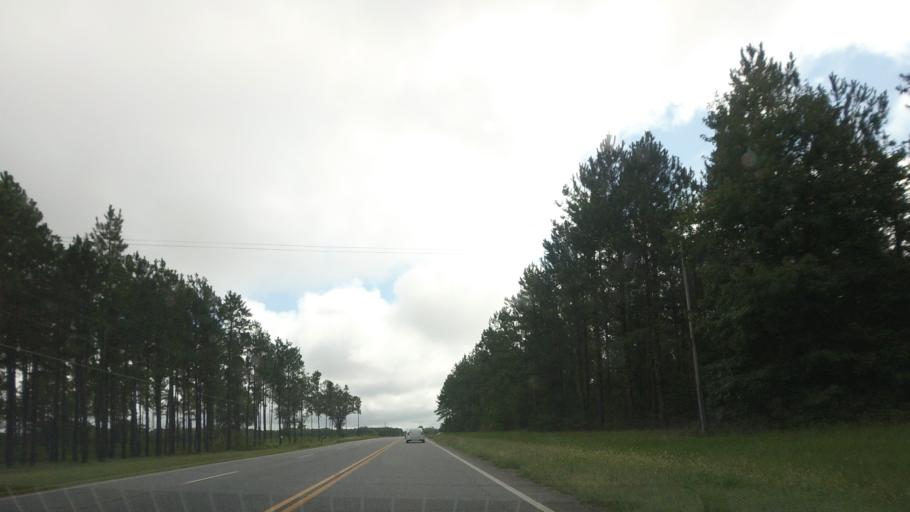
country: US
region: Georgia
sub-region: Laurens County
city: Dublin
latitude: 32.5505
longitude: -83.0051
